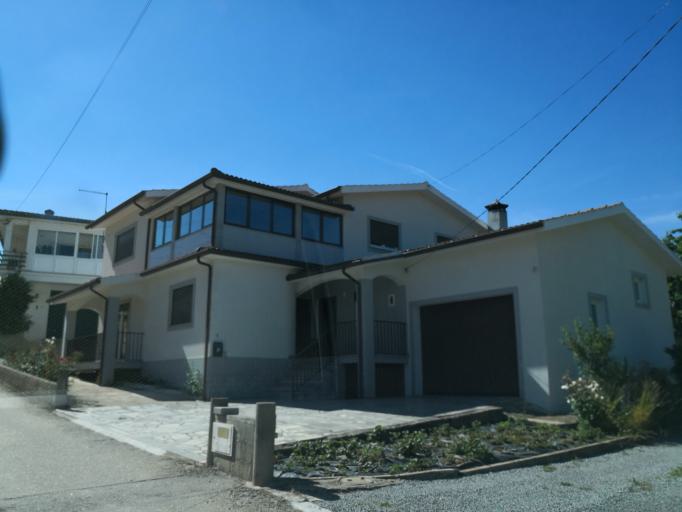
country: PT
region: Vila Real
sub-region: Vila Real
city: Vila Real
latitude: 41.2852
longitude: -7.6945
